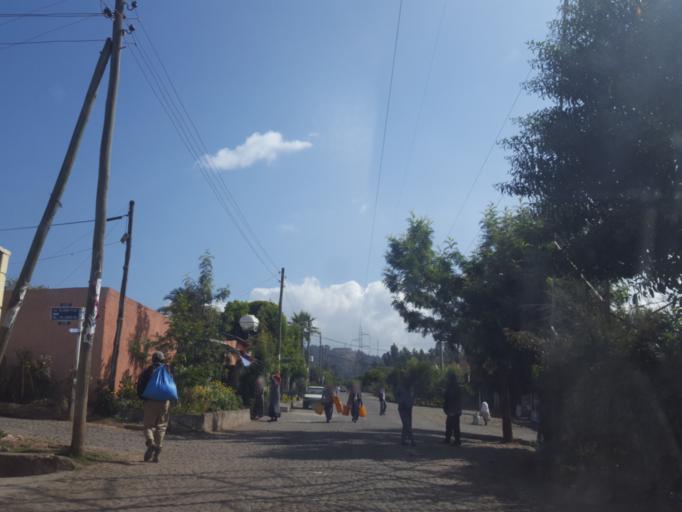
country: ET
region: Adis Abeba
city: Addis Ababa
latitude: 9.0672
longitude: 38.7176
